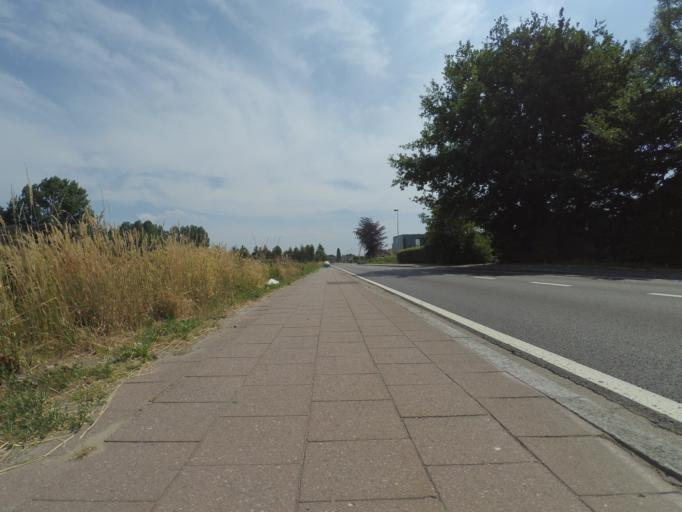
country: BE
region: Flanders
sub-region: Provincie Antwerpen
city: Wuustwezel
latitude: 51.4016
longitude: 4.6258
